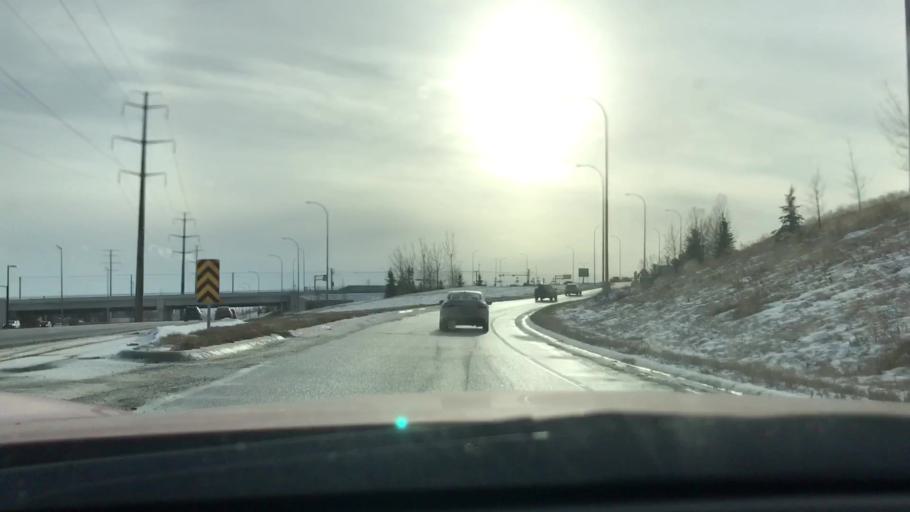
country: CA
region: Alberta
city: Calgary
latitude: 51.0425
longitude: -114.1648
